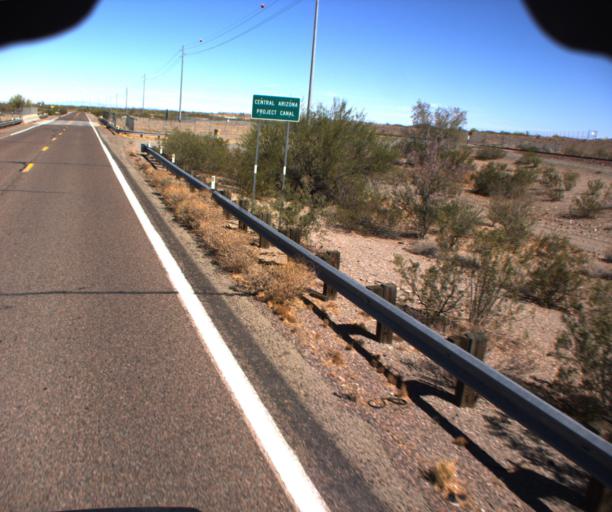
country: US
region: Arizona
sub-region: La Paz County
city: Salome
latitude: 33.7659
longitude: -113.7880
